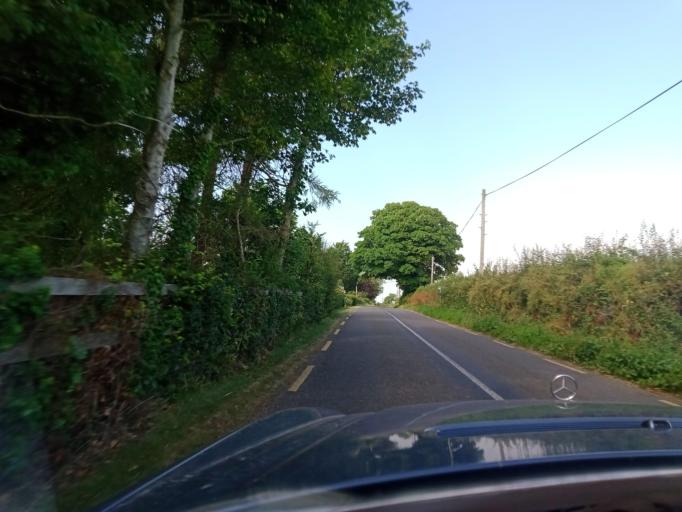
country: IE
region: Leinster
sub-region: Kilkenny
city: Callan
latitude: 52.5139
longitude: -7.3122
